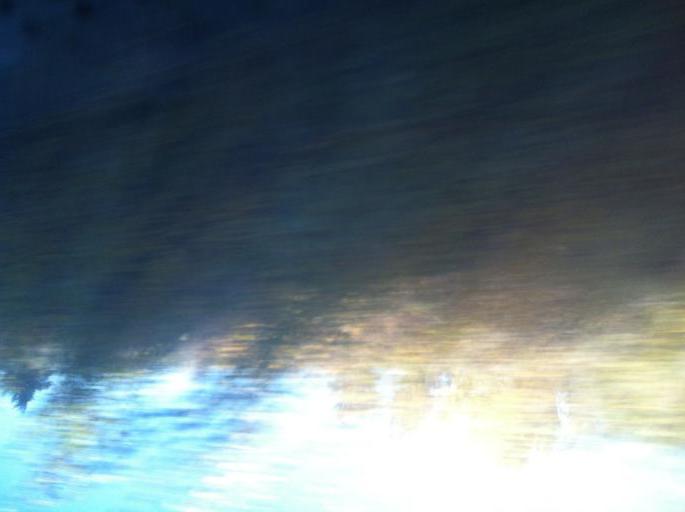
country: ES
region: Castille and Leon
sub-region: Provincia de Palencia
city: Reinoso de Cerrato
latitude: 42.0023
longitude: -4.3582
